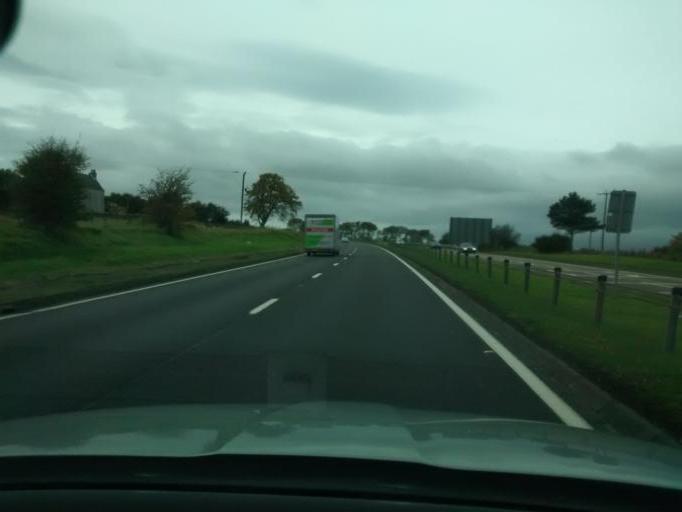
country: GB
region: Scotland
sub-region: Perth and Kinross
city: Perth
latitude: 56.3877
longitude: -3.4922
